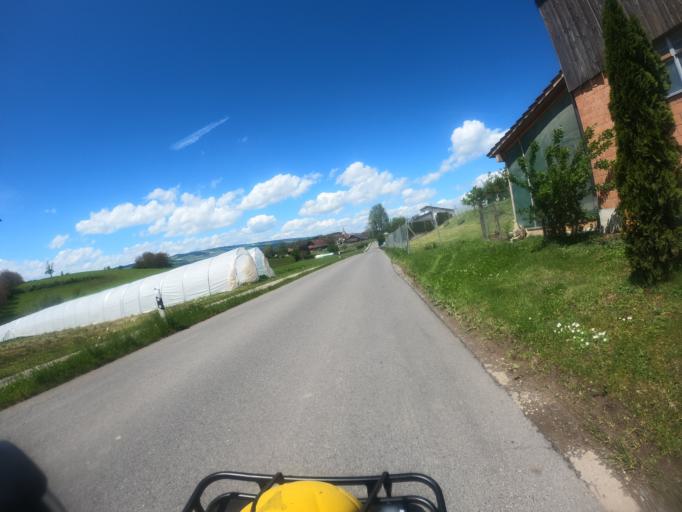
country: CH
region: Zurich
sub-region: Bezirk Affoltern
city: Knonau
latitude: 47.2104
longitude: 8.4575
